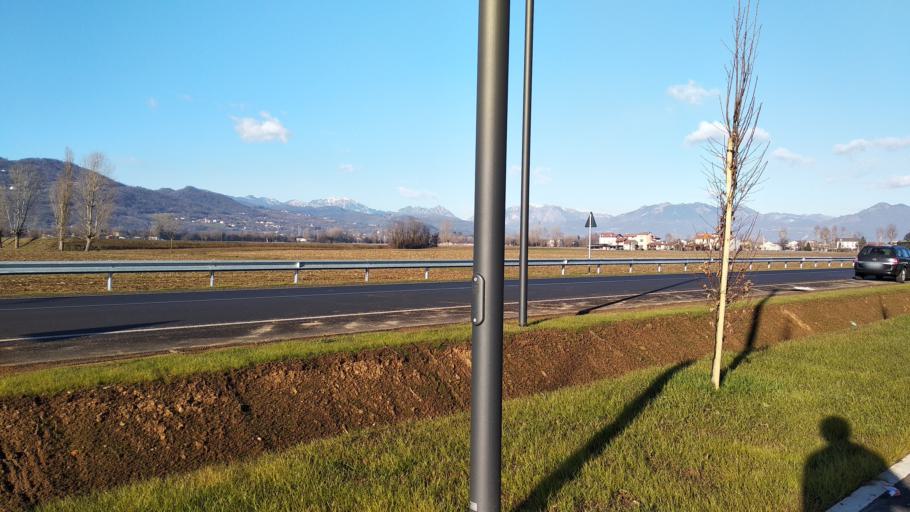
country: IT
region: Veneto
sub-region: Provincia di Vicenza
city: Motta
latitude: 45.6012
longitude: 11.4907
